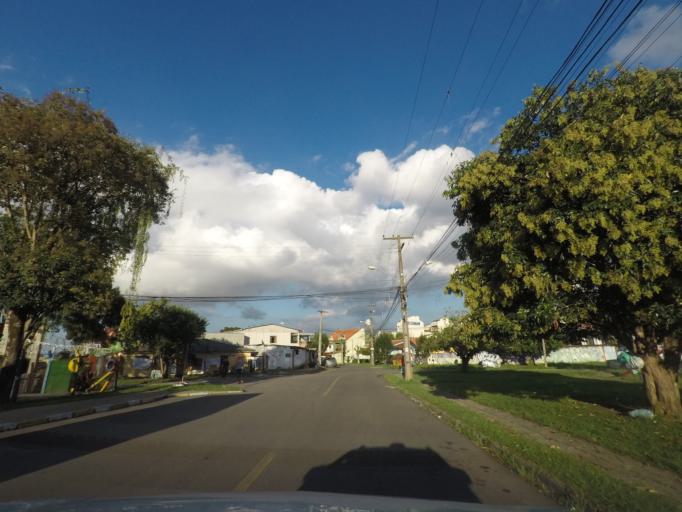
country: BR
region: Parana
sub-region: Sao Jose Dos Pinhais
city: Sao Jose dos Pinhais
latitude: -25.4988
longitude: -49.2618
